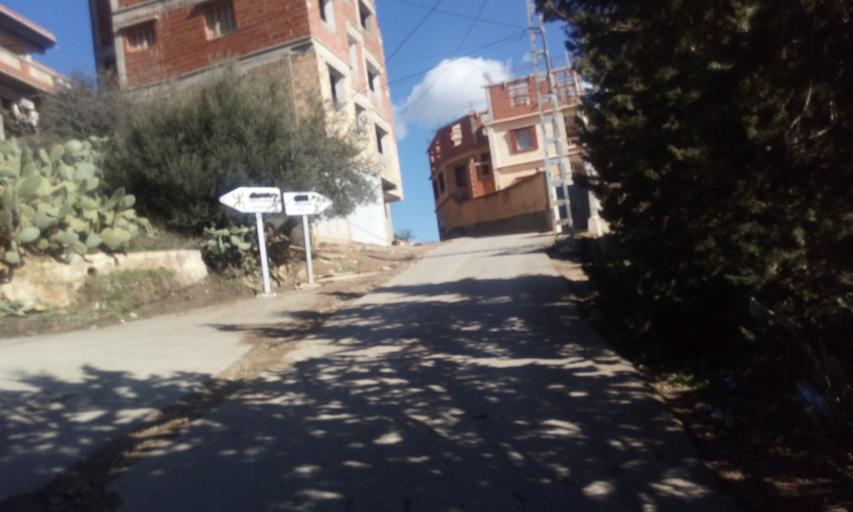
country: DZ
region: Tizi Ouzou
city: Chemini
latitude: 36.6045
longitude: 4.6361
